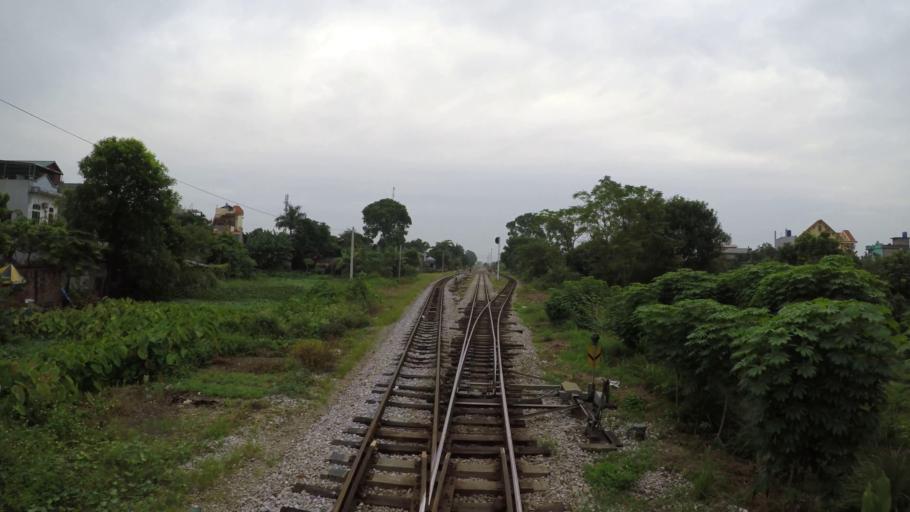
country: VN
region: Hai Duong
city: Ke Sat
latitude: 20.9666
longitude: 106.1469
